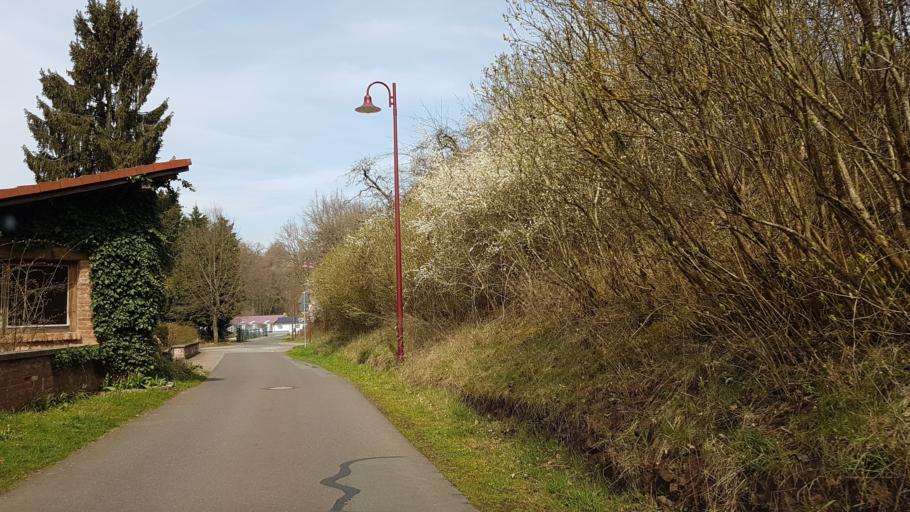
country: DE
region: Rheinland-Pfalz
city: Nanzdietschweiler
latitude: 49.4391
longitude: 7.4359
